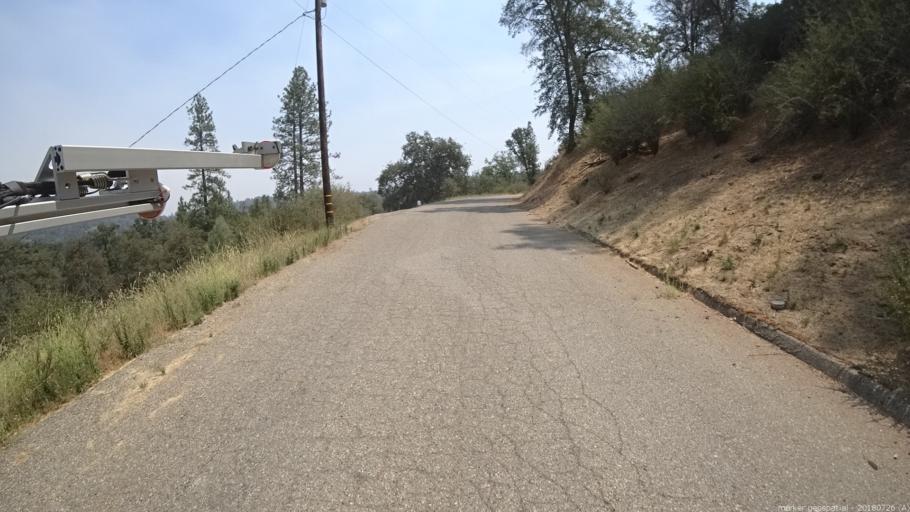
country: US
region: California
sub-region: Madera County
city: Oakhurst
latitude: 37.2853
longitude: -119.6522
